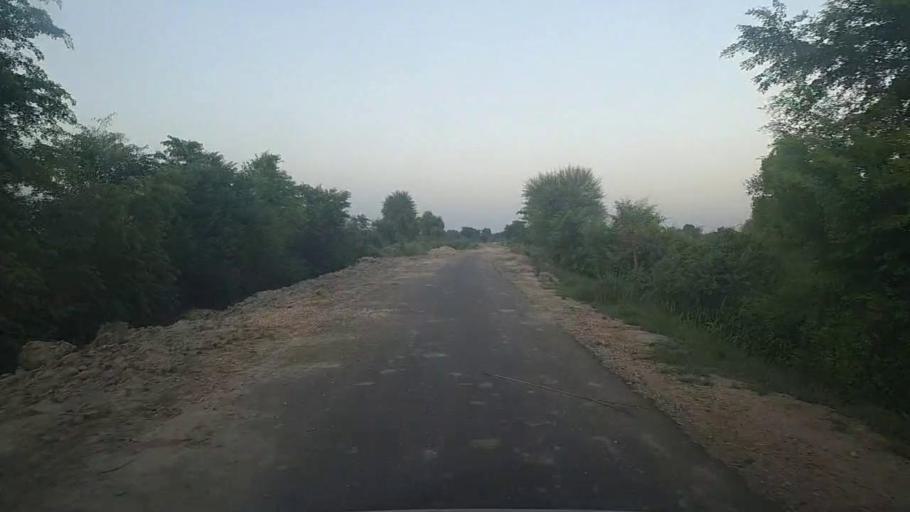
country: PK
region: Sindh
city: Khairpur
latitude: 28.0918
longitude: 69.7310
